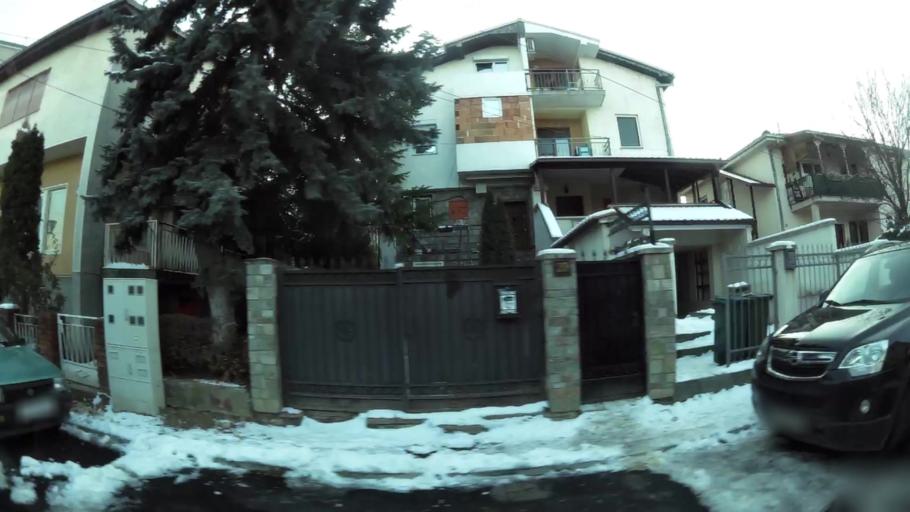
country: MK
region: Karpos
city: Skopje
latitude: 41.9914
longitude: 21.4083
